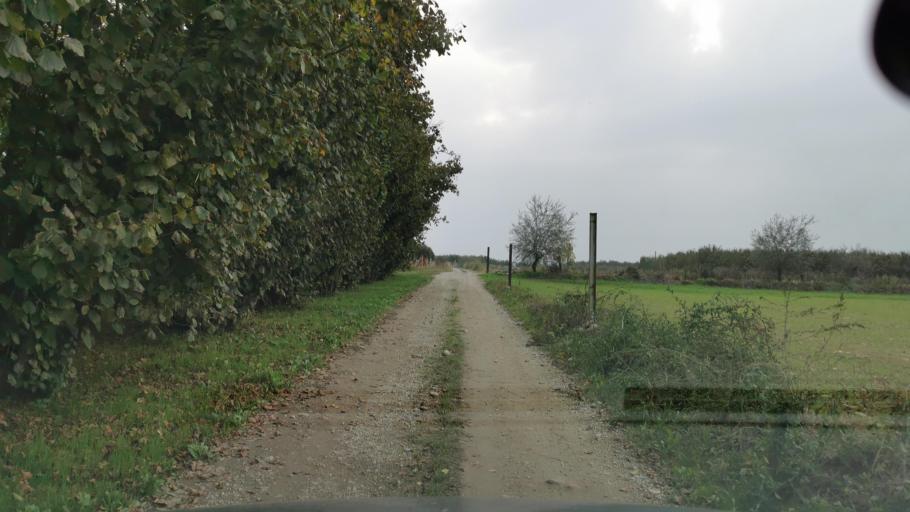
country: IT
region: Piedmont
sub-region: Provincia di Cuneo
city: Cinzano
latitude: 44.6870
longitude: 7.9132
